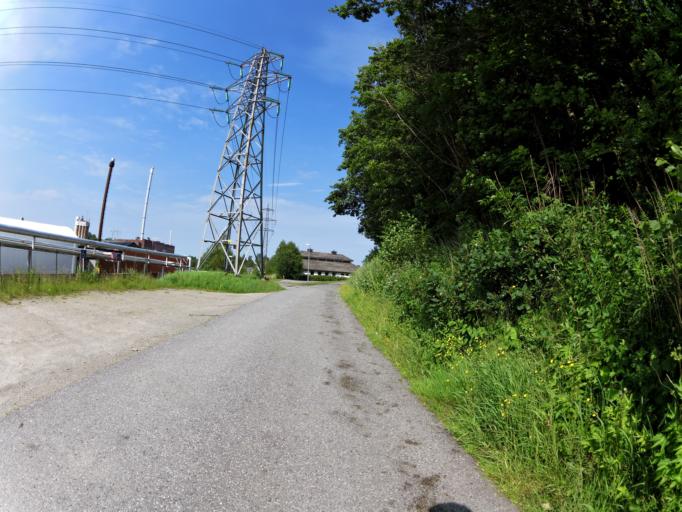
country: NO
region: Ostfold
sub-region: Sarpsborg
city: Sarpsborg
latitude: 59.2728
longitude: 11.1277
